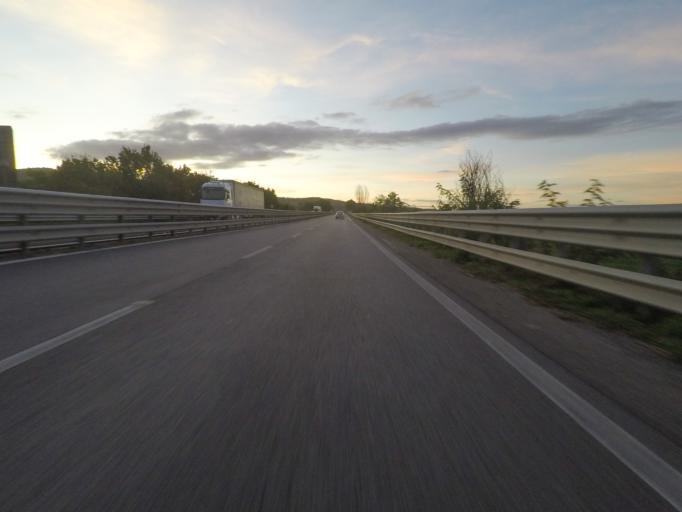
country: IT
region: Tuscany
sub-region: Provincia di Siena
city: Sinalunga
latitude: 43.2236
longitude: 11.7482
